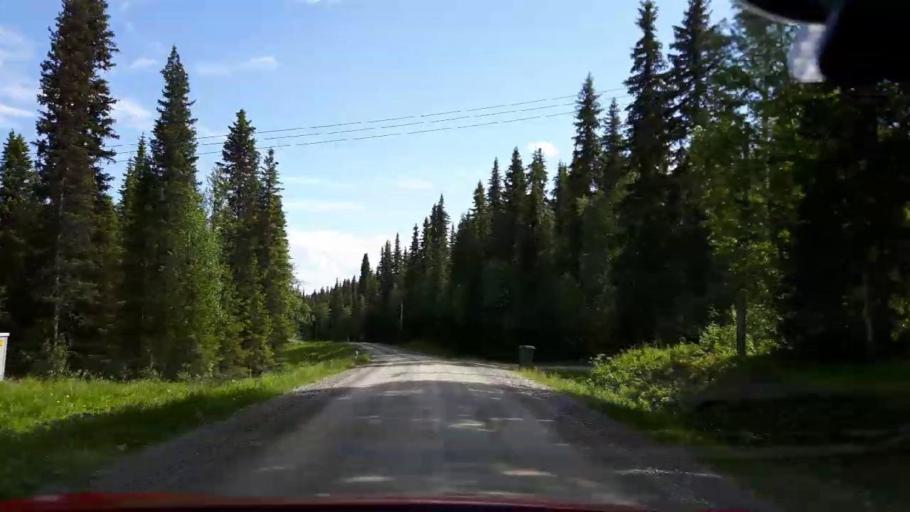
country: SE
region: Jaemtland
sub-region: Krokoms Kommun
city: Valla
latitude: 63.7992
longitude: 14.0460
